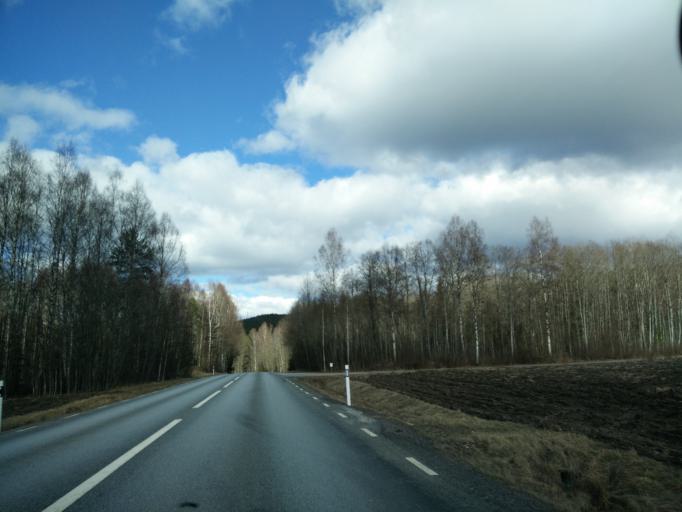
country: SE
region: Vaermland
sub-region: Munkfors Kommun
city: Munkfors
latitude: 59.8814
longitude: 13.5641
